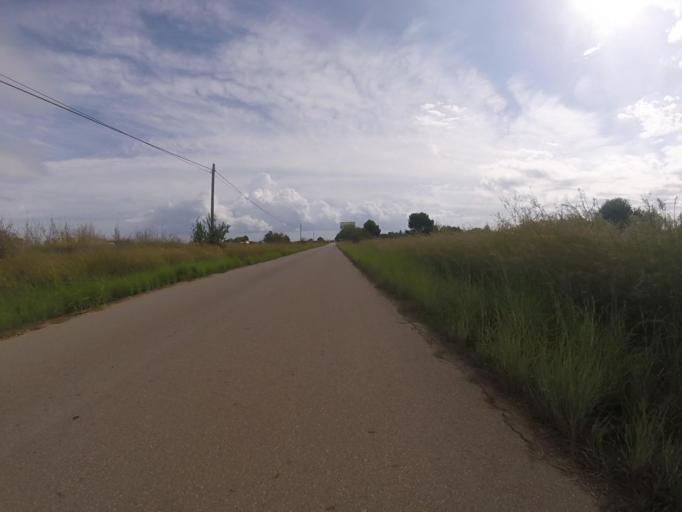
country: ES
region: Valencia
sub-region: Provincia de Castello
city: Orpesa/Oropesa del Mar
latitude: 40.1313
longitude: 0.1554
